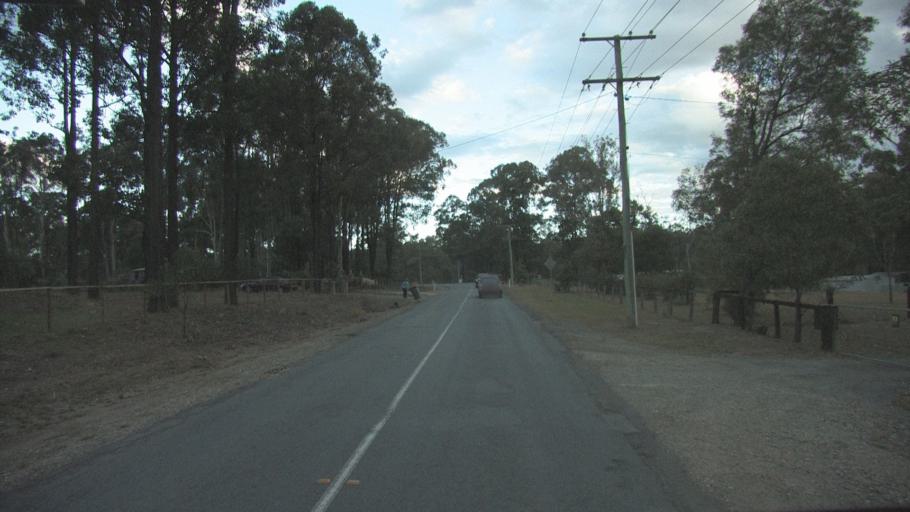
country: AU
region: Queensland
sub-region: Logan
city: Chambers Flat
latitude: -27.7881
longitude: 153.1359
